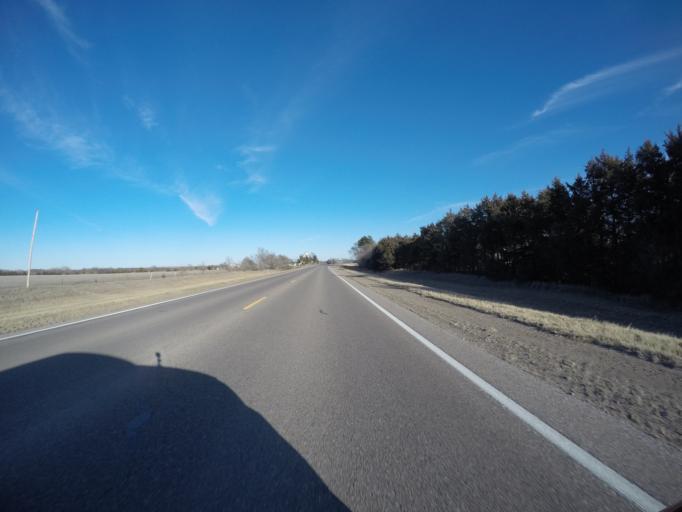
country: US
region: Nebraska
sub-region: Gage County
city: Wymore
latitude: 40.1395
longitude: -96.6831
